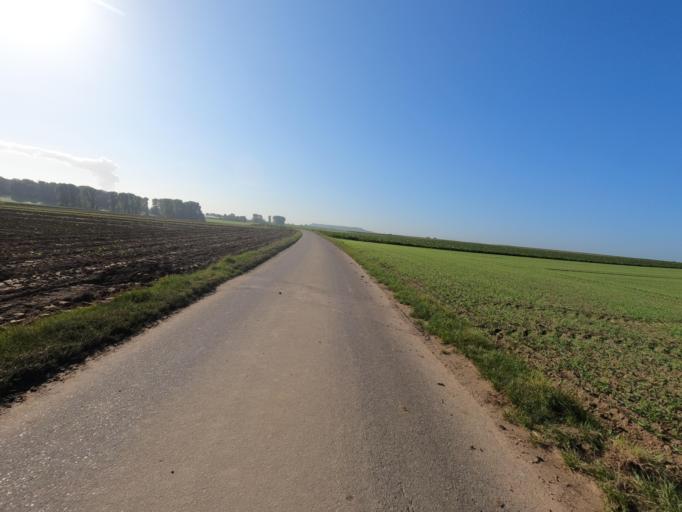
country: DE
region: North Rhine-Westphalia
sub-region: Regierungsbezirk Koln
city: Linnich
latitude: 50.9725
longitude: 6.2543
